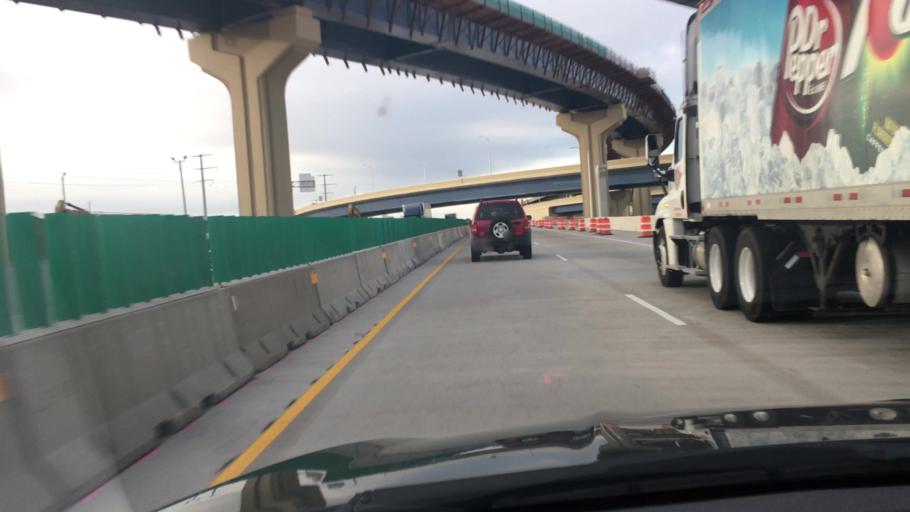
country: US
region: Wisconsin
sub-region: Milwaukee County
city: West Allis
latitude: 43.0274
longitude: -88.0354
